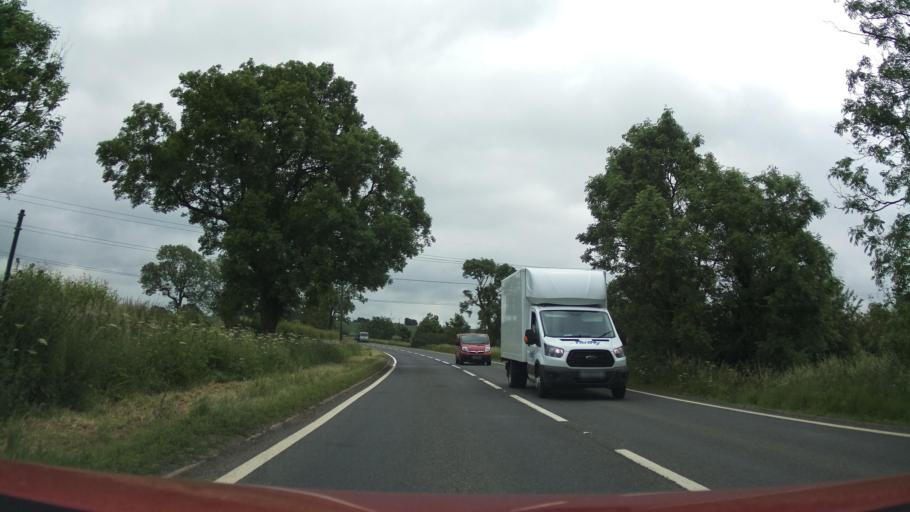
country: GB
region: England
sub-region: Leicestershire
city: Houghton on the Hill
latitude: 52.6153
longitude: -0.8967
